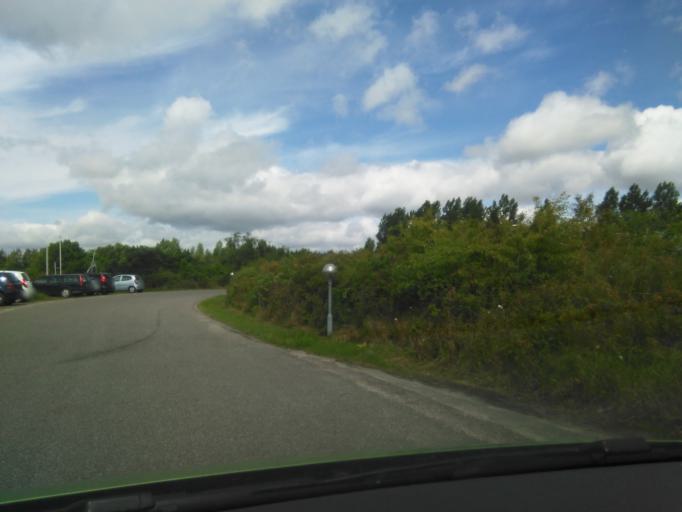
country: DK
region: Central Jutland
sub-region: Arhus Kommune
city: Logten
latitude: 56.2451
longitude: 10.3403
